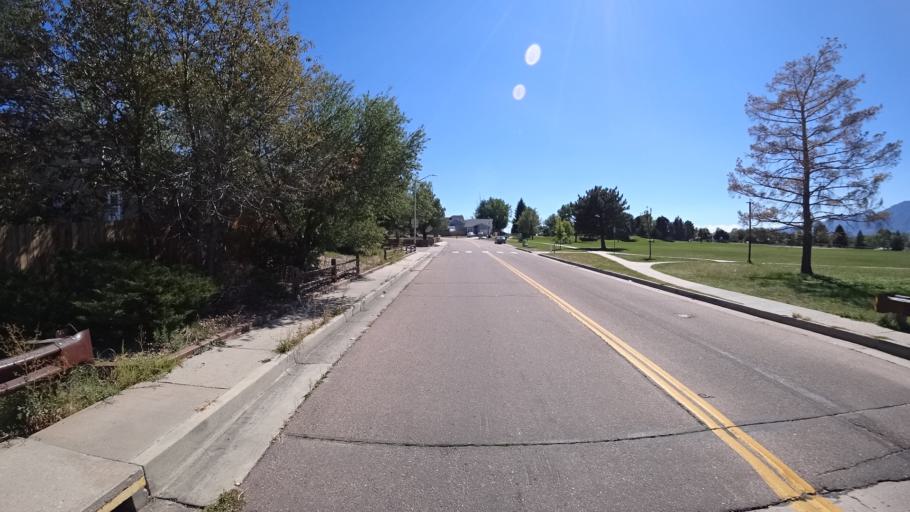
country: US
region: Colorado
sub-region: El Paso County
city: Stratmoor
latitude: 38.7866
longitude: -104.7470
